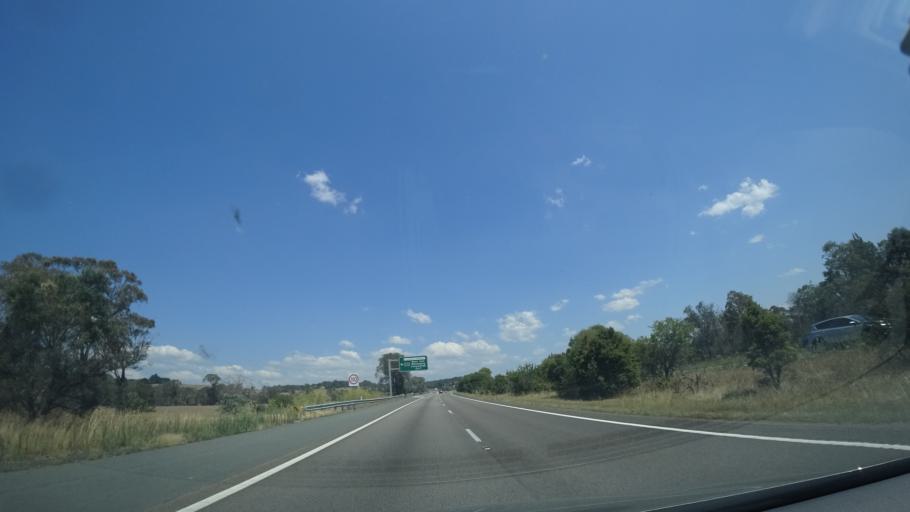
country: AU
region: New South Wales
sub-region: Wingecarribee
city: Bundanoon
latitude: -34.5807
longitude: 150.2525
